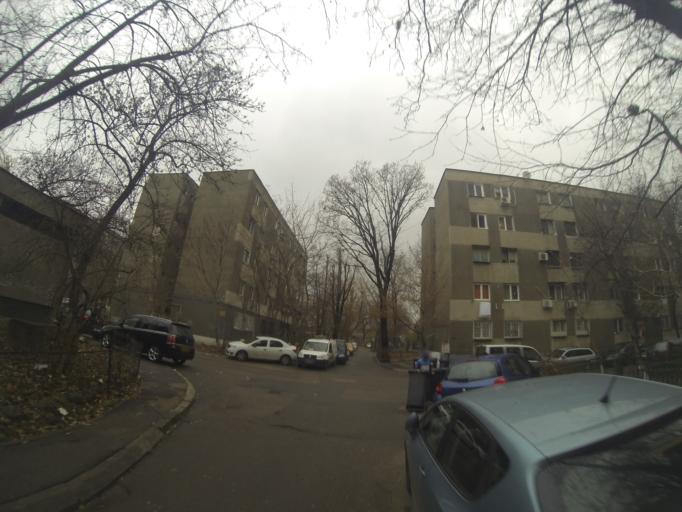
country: RO
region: Bucuresti
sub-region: Municipiul Bucuresti
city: Bucuresti
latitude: 44.4067
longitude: 26.0714
